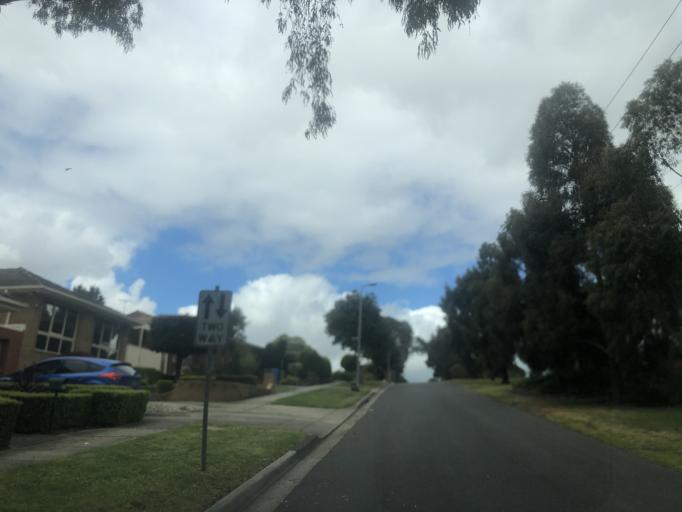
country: AU
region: Victoria
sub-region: Casey
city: Endeavour Hills
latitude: -37.9722
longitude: 145.2441
